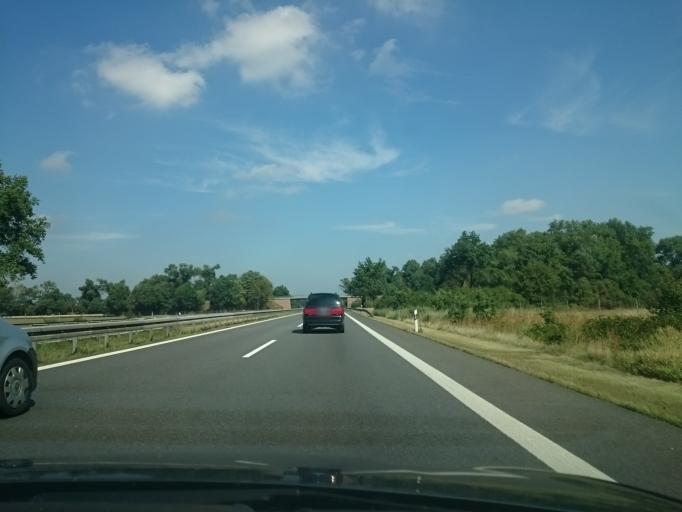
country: DE
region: Brandenburg
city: Calau
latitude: 51.7555
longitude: 13.8633
